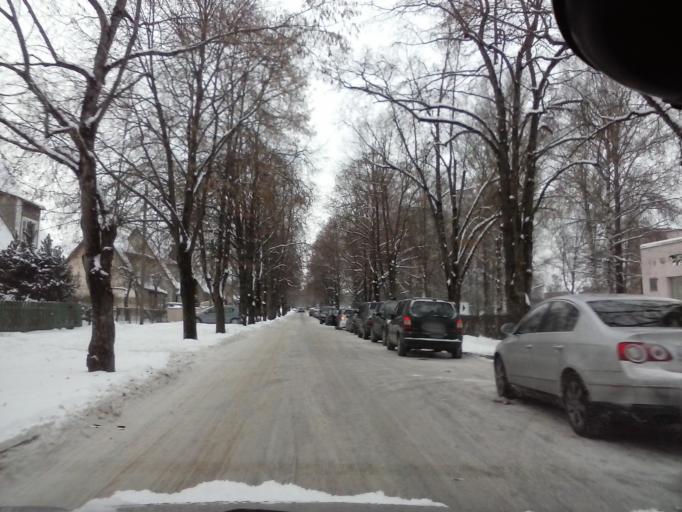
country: EE
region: Tartu
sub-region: Tartu linn
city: Tartu
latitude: 58.3671
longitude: 26.6991
